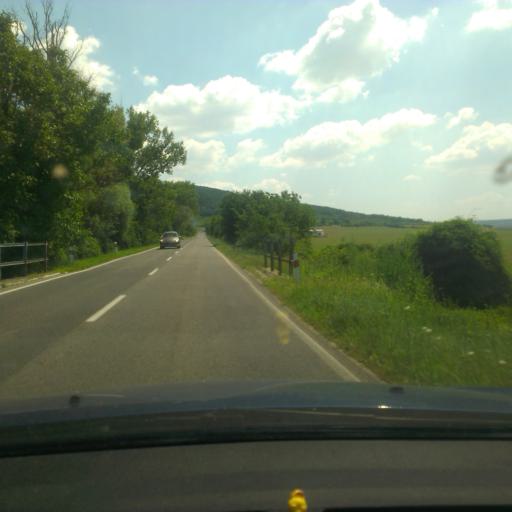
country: SK
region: Trnavsky
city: Hlohovec
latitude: 48.4669
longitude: 17.8127
